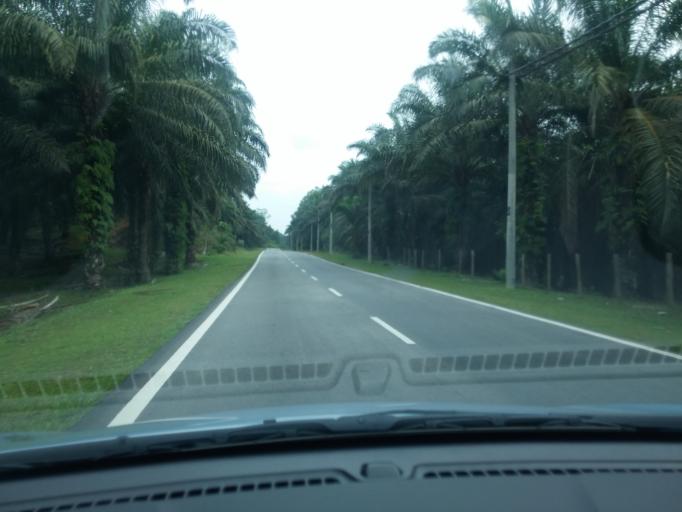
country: MY
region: Pahang
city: Kuantan
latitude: 3.8565
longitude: 103.1634
